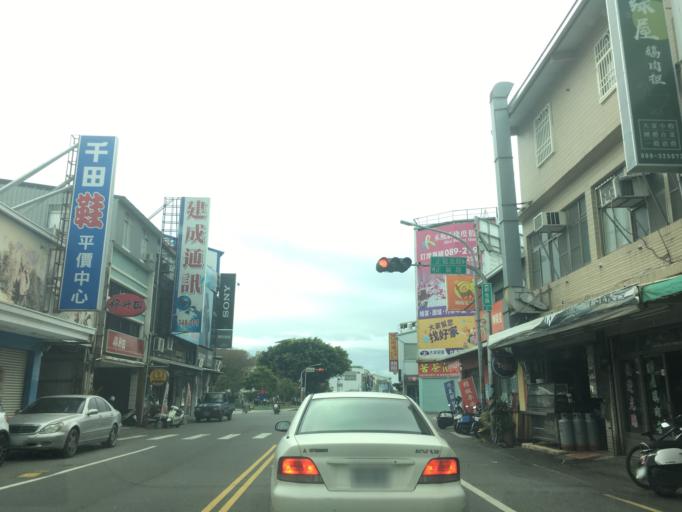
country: TW
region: Taiwan
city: Taitung City
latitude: 22.7576
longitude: 121.1425
